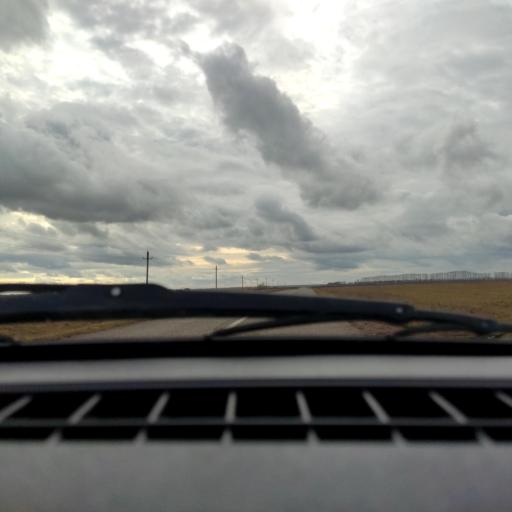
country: RU
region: Bashkortostan
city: Asanovo
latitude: 54.9512
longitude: 55.5311
